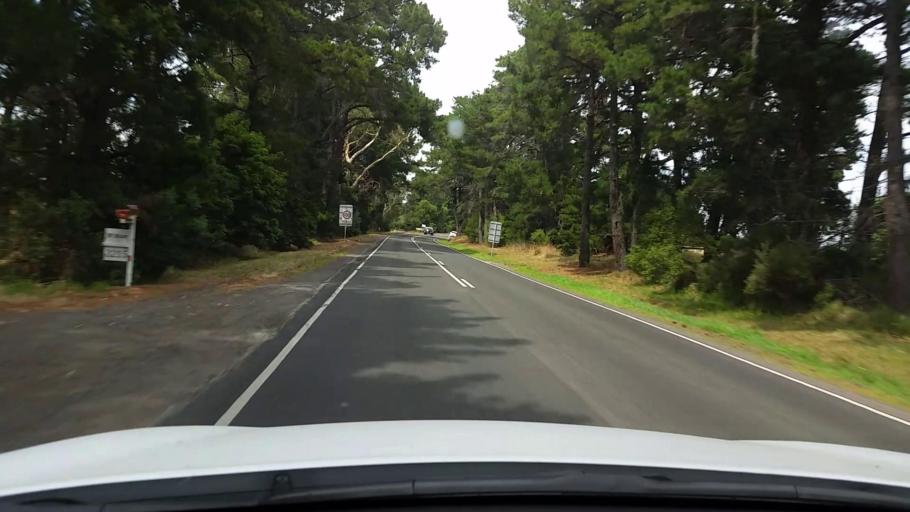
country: AU
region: Victoria
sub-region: Mornington Peninsula
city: Balnarring
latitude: -38.3802
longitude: 145.1103
